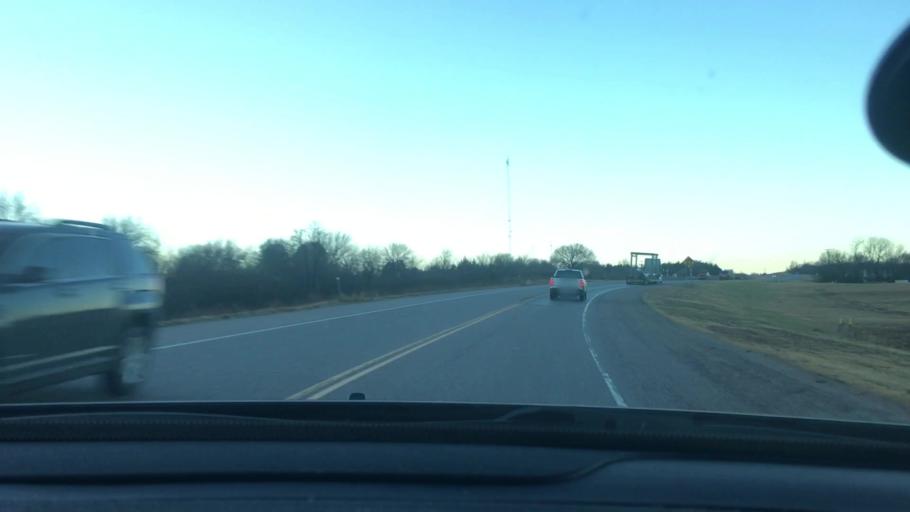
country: US
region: Oklahoma
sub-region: Pontotoc County
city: Ada
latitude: 34.7502
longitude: -96.7020
